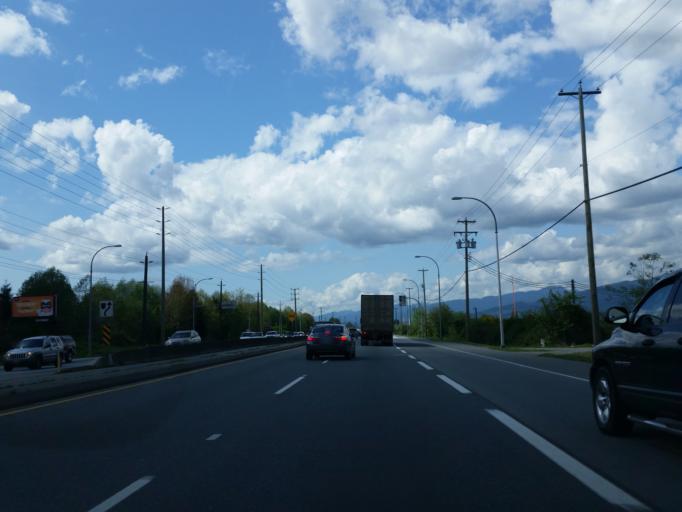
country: CA
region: British Columbia
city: Pitt Meadows
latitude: 49.2353
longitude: -122.7001
